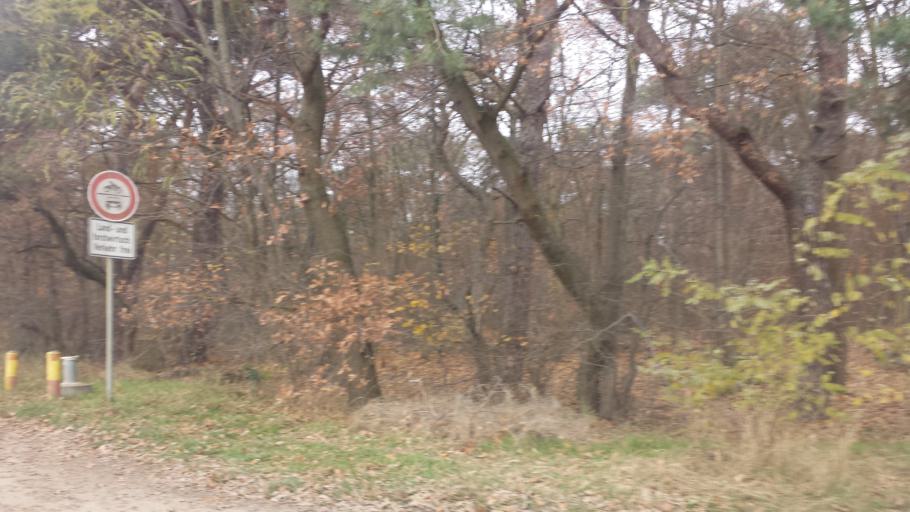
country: DE
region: Hesse
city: Lampertheim
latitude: 49.6082
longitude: 8.4915
